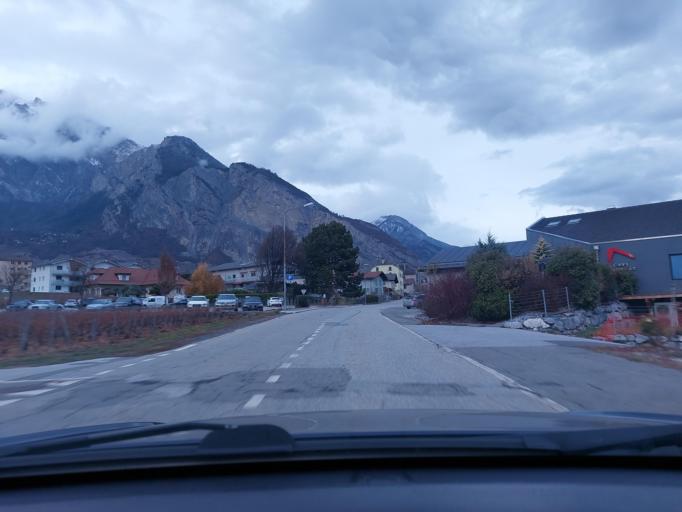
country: CH
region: Valais
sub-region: Conthey District
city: Chamoson
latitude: 46.1895
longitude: 7.2357
